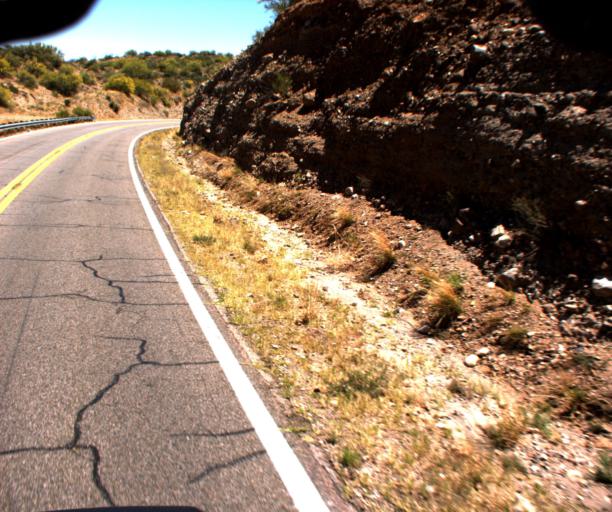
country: US
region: Arizona
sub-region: Pinal County
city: Kearny
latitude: 33.1687
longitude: -110.8063
